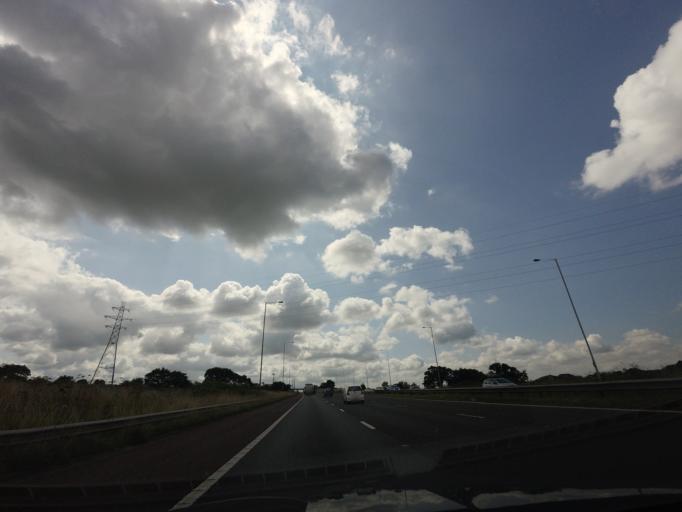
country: GB
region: England
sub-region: Lancashire
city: Euxton
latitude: 53.6478
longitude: -2.6917
